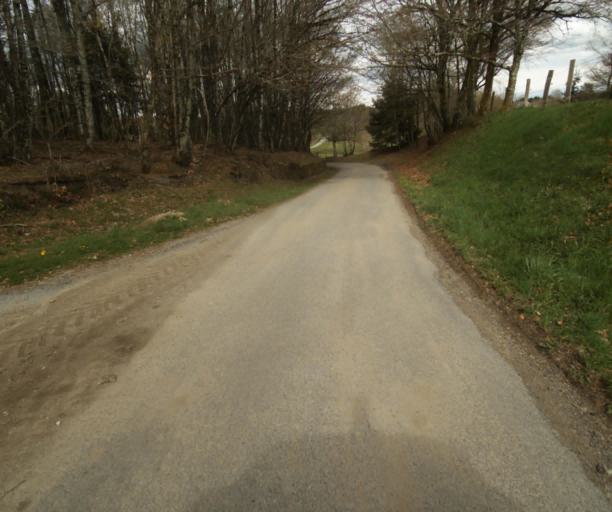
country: FR
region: Limousin
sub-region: Departement de la Correze
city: Argentat
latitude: 45.1975
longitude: 1.9275
